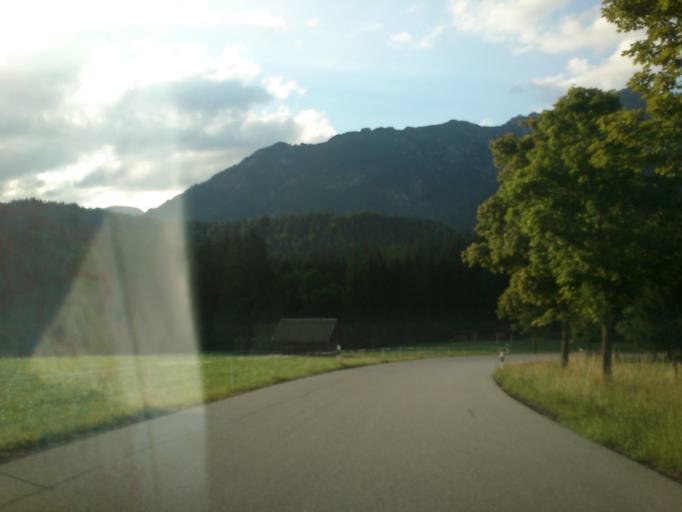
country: DE
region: Bavaria
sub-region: Upper Bavaria
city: Grainau
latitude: 47.4691
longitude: 11.0065
